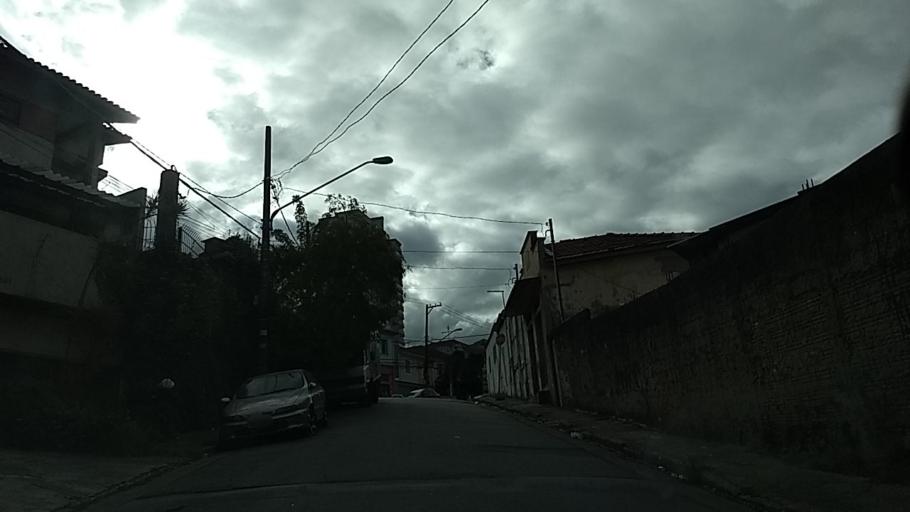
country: BR
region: Sao Paulo
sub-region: Sao Paulo
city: Sao Paulo
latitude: -23.4995
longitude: -46.5957
